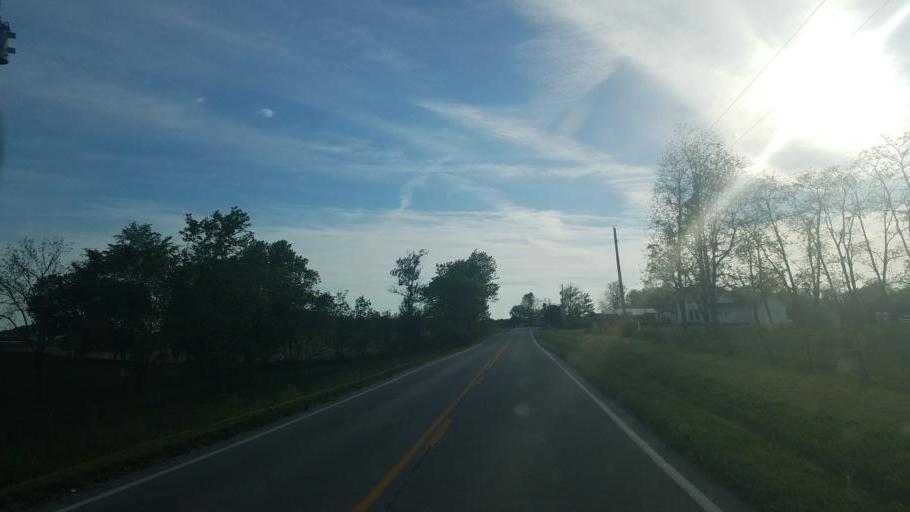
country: US
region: Ohio
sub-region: Ross County
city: Frankfort
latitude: 39.4237
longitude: -83.2589
